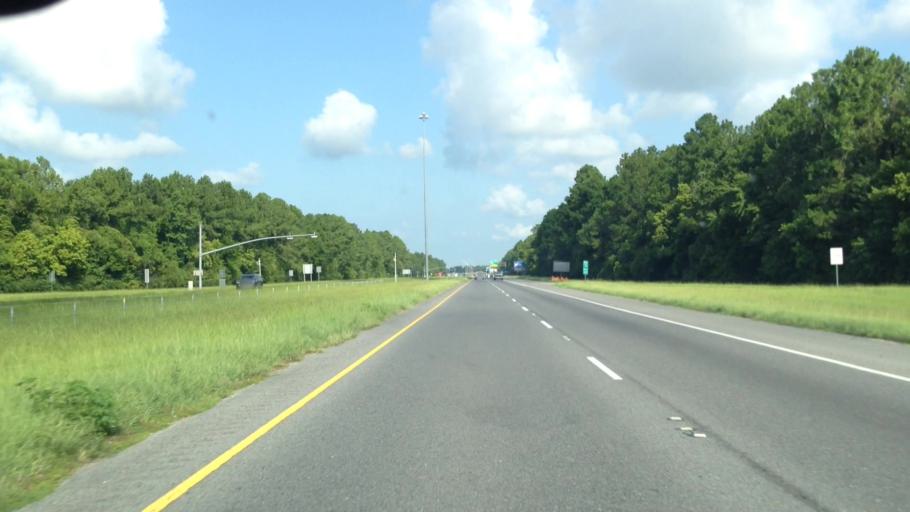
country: US
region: Louisiana
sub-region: Saint John the Baptist Parish
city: Laplace
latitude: 30.1006
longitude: -90.4822
